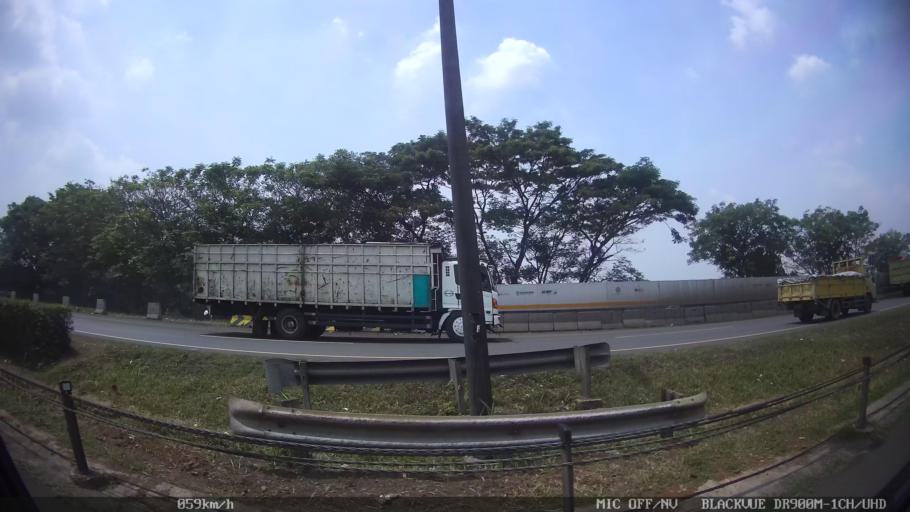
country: ID
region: Banten
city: Serang
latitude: -6.1335
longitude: 106.2079
